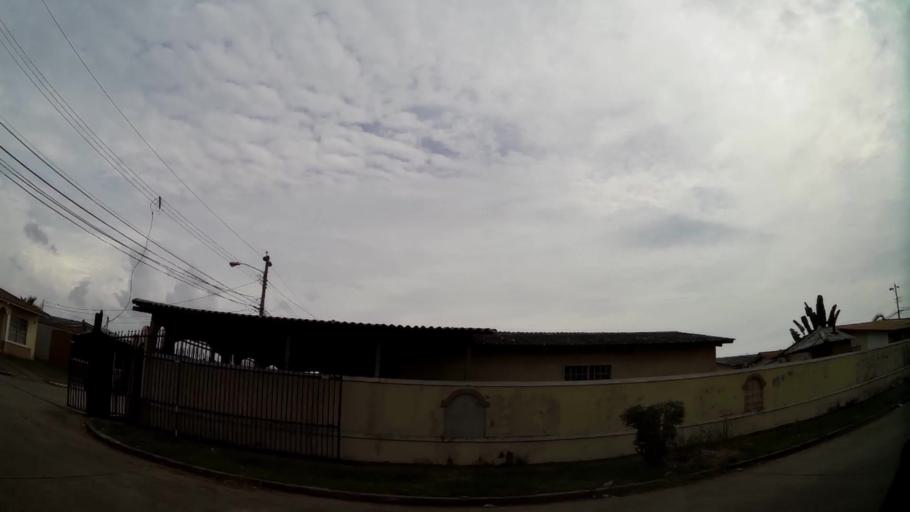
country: PA
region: Panama
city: Tocumen
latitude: 9.0432
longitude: -79.4050
